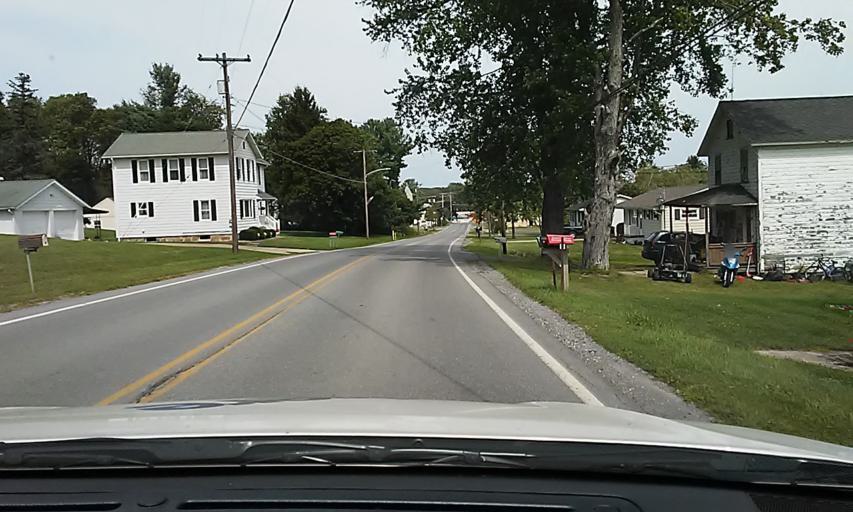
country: US
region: Pennsylvania
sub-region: Elk County
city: Saint Marys
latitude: 41.3588
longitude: -78.6106
